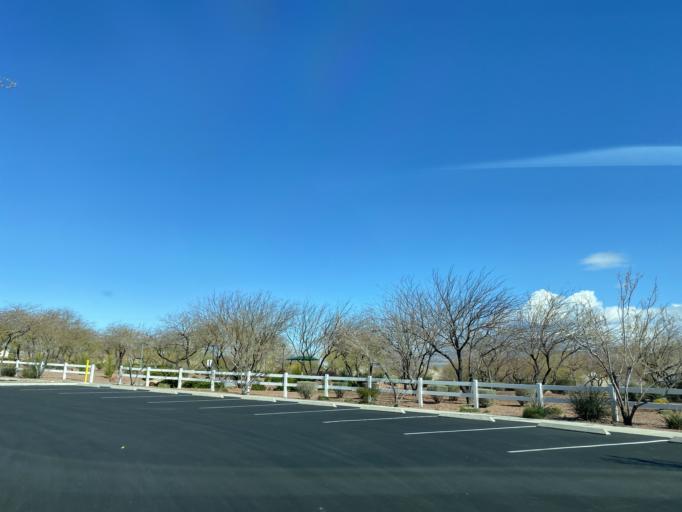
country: US
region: Nevada
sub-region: Clark County
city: North Las Vegas
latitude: 36.3320
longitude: -115.2734
